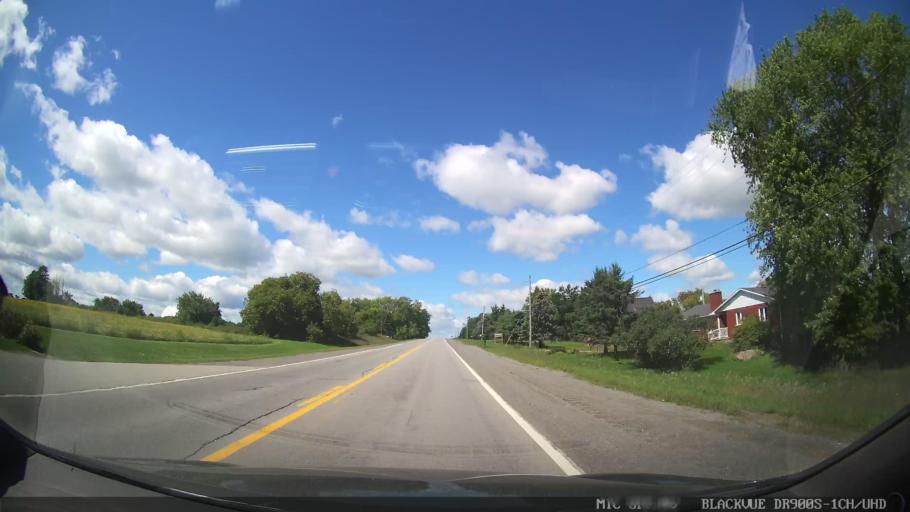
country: CA
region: Ontario
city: Bells Corners
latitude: 45.1201
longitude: -75.7018
